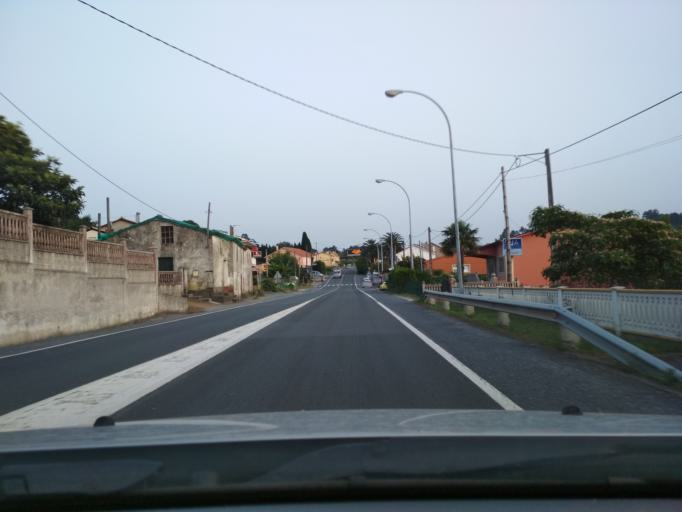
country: ES
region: Galicia
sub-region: Provincia da Coruna
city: Culleredo
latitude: 43.2814
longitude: -8.3666
